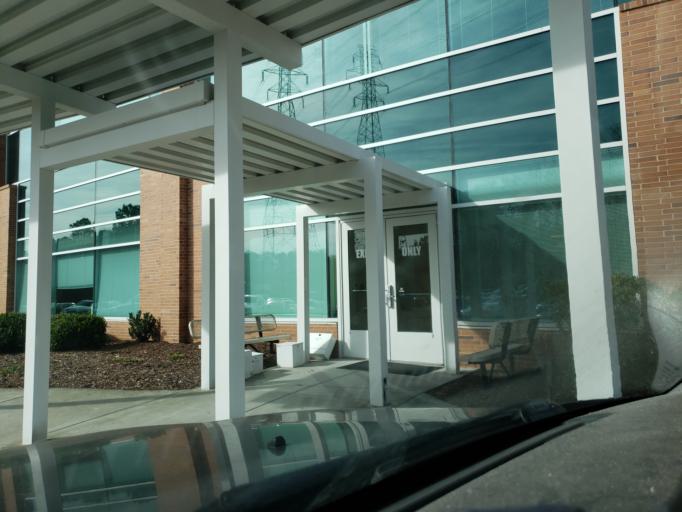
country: US
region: North Carolina
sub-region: Durham County
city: Durham
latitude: 35.9107
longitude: -78.9289
